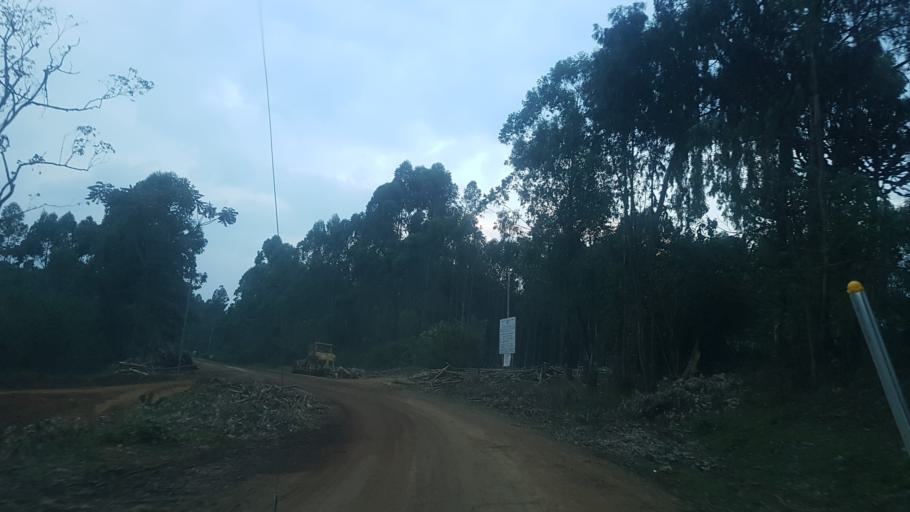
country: ET
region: Oromiya
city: Gore
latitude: 7.7905
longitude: 35.4559
